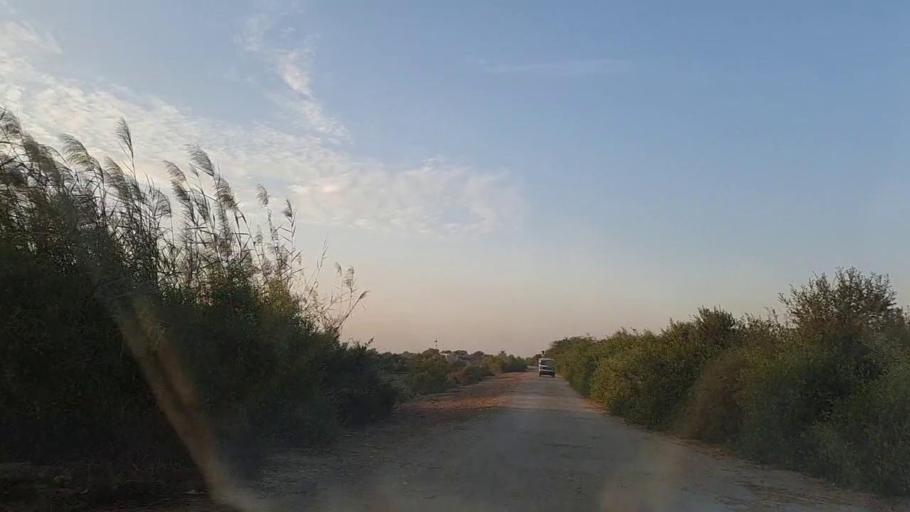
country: PK
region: Sindh
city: Chuhar Jamali
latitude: 24.4534
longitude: 68.1175
